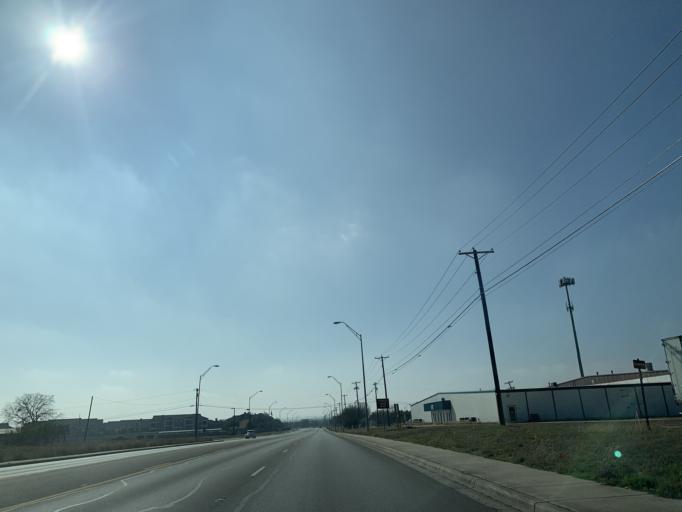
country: US
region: Texas
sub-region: Williamson County
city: Round Rock
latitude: 30.5262
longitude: -97.6534
